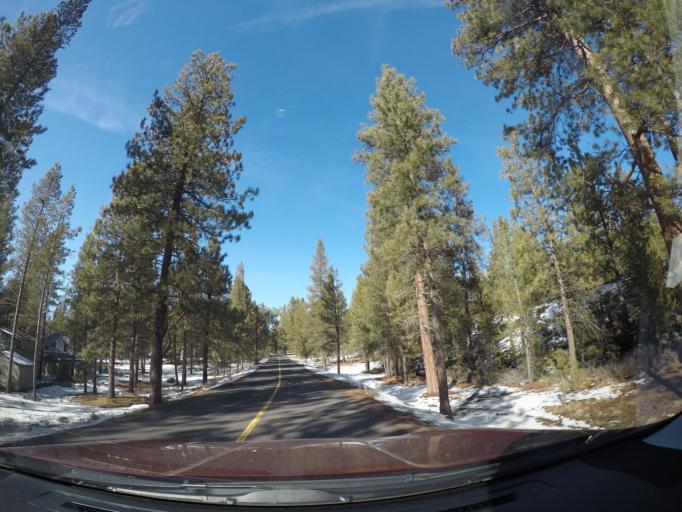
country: US
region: Oregon
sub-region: Deschutes County
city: Sunriver
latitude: 43.8725
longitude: -121.4310
